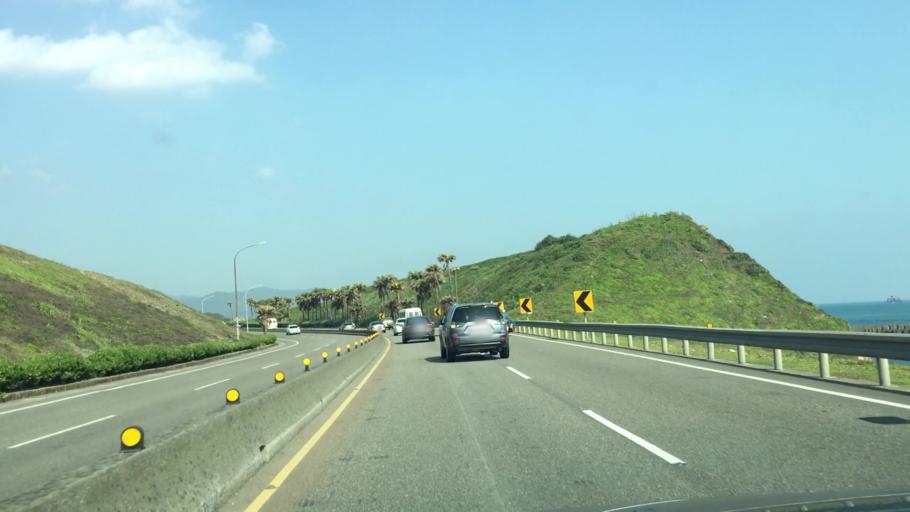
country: TW
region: Taiwan
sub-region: Keelung
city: Keelung
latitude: 25.2045
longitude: 121.6668
